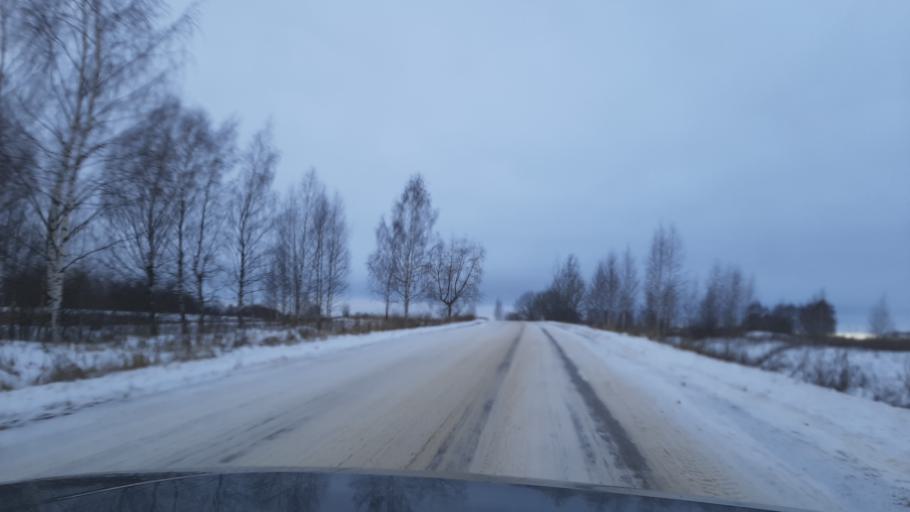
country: RU
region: Kostroma
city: Volgorechensk
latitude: 57.4369
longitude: 41.0795
